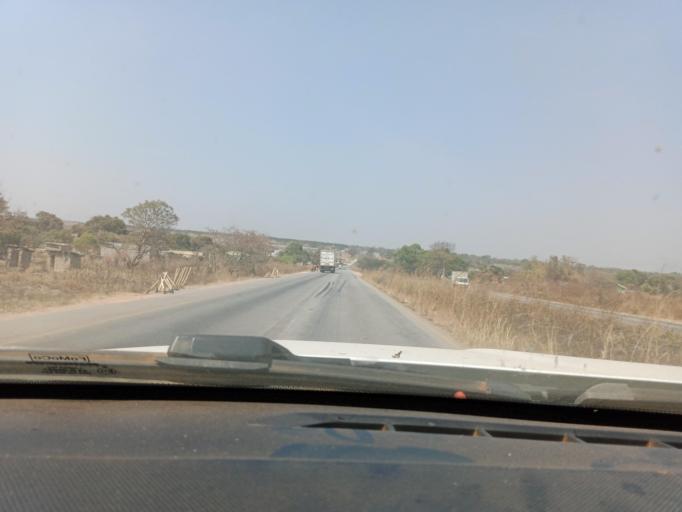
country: ZM
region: Copperbelt
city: Luanshya
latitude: -13.0295
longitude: 28.4491
